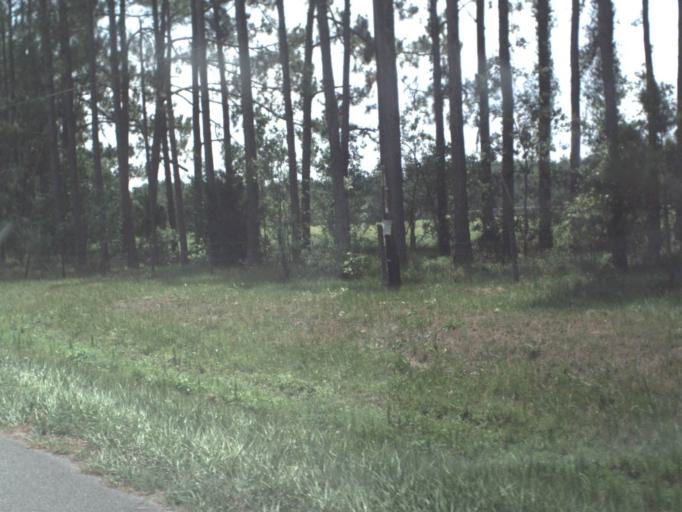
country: US
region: Florida
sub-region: Nassau County
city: Nassau Village-Ratliff
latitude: 30.5171
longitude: -81.7622
